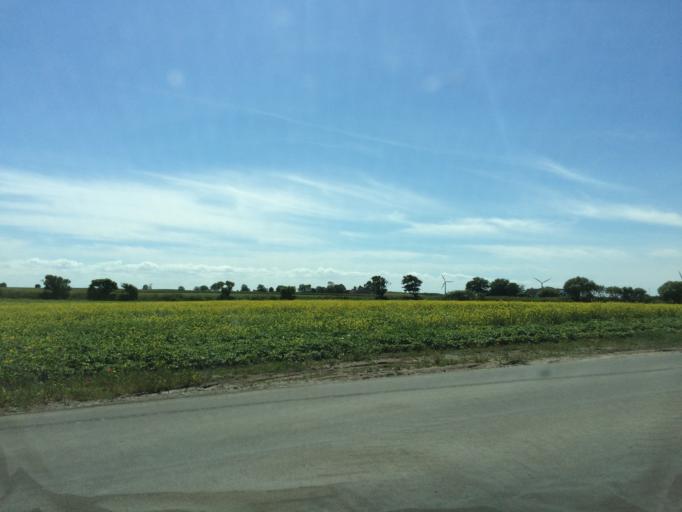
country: DK
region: Central Jutland
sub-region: Samso Kommune
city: Tranebjerg
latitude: 55.8079
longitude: 10.6379
